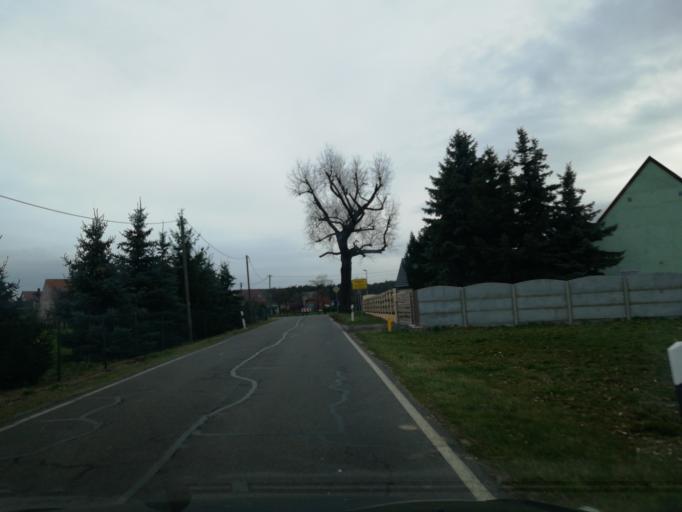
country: DE
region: Brandenburg
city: Calau
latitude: 51.7319
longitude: 14.0158
